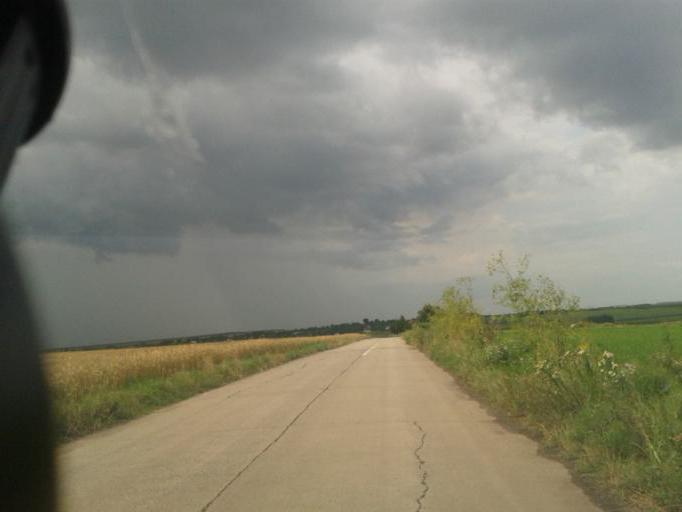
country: RO
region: Ialomita
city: Dragoesti-Snagov
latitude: 44.5439
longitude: 26.4719
